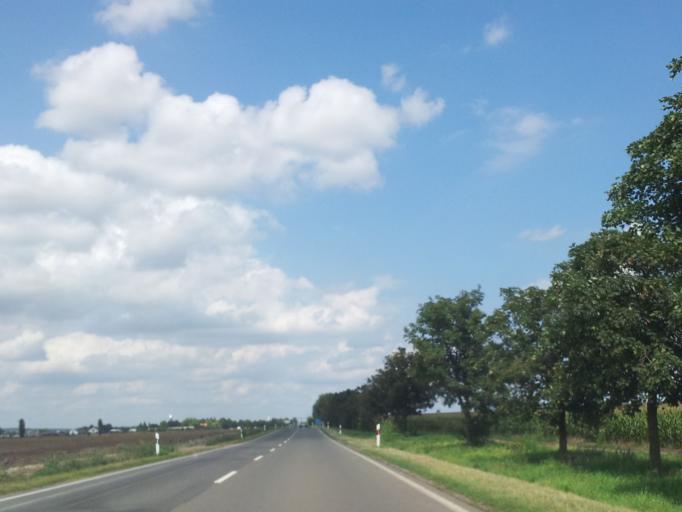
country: HU
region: Baranya
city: Mohacs
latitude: 45.9660
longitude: 18.6720
